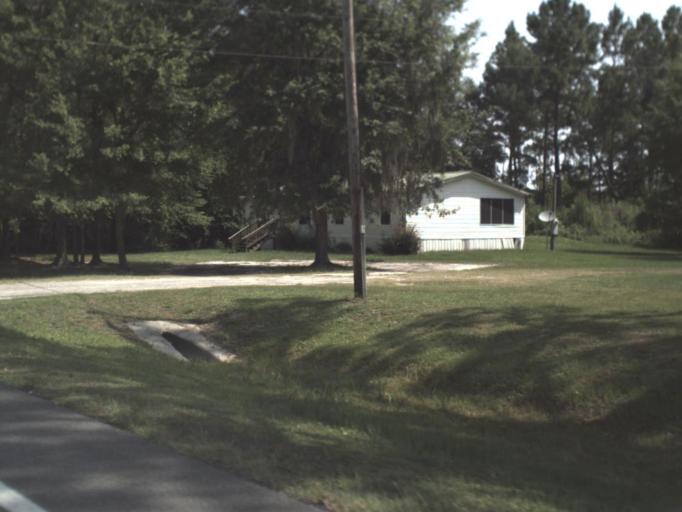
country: US
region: Florida
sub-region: Hamilton County
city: Jasper
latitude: 30.5379
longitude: -82.9729
